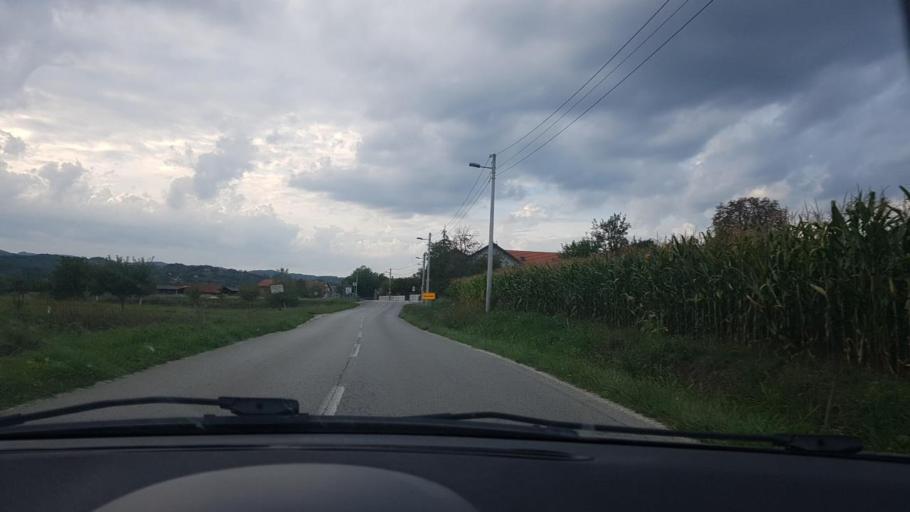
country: HR
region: Grad Zagreb
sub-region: Sesvete
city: Sesvete
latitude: 45.8933
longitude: 16.1698
